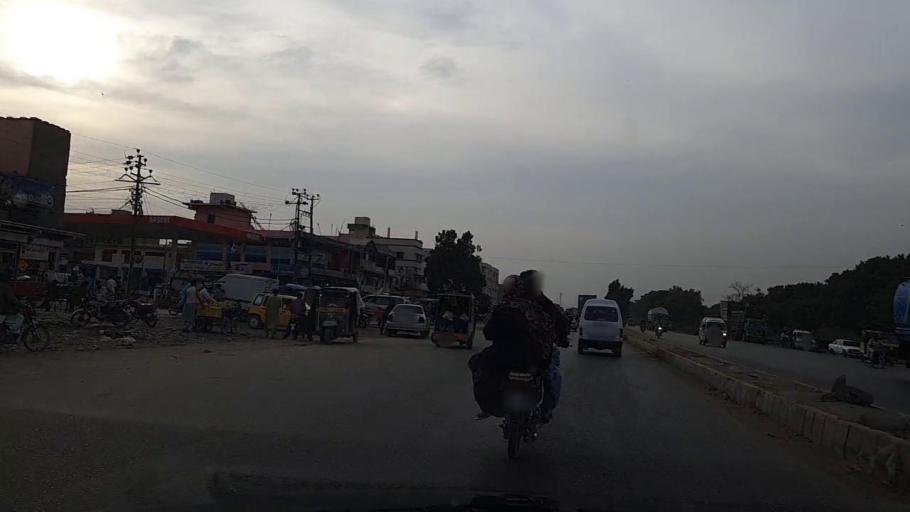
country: PK
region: Sindh
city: Malir Cantonment
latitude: 24.8600
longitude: 67.3358
